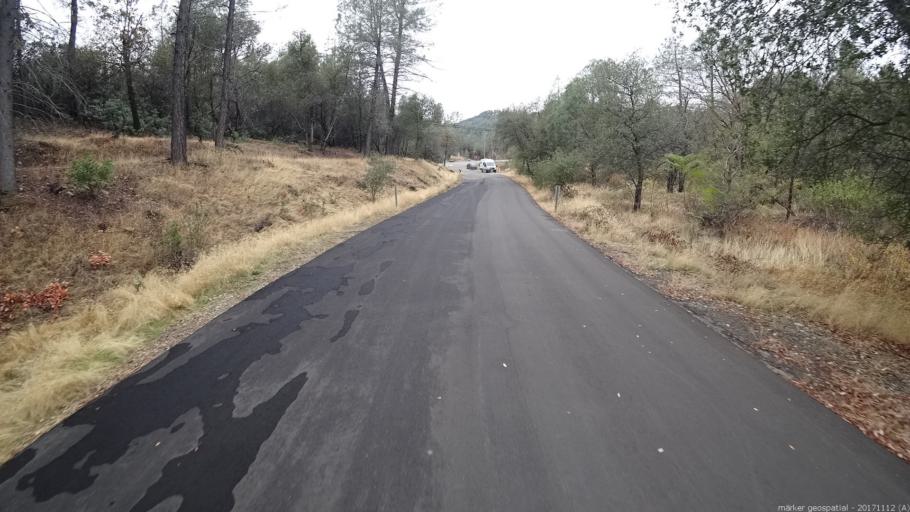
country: US
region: California
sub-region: Shasta County
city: Shasta
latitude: 40.5927
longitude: -122.4829
